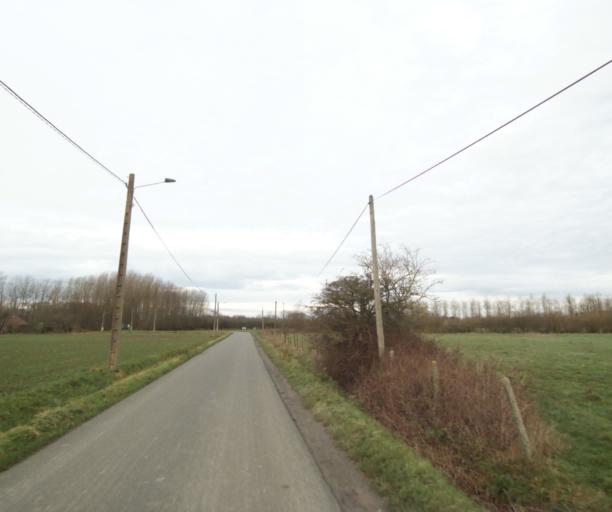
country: FR
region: Nord-Pas-de-Calais
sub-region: Departement du Nord
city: Bruille-Saint-Amand
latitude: 50.4828
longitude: 3.5037
